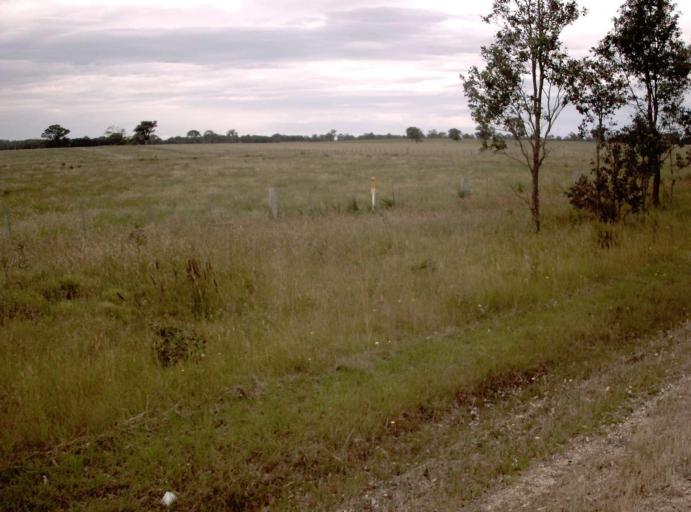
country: AU
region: Victoria
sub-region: East Gippsland
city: Bairnsdale
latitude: -37.7992
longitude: 147.3537
